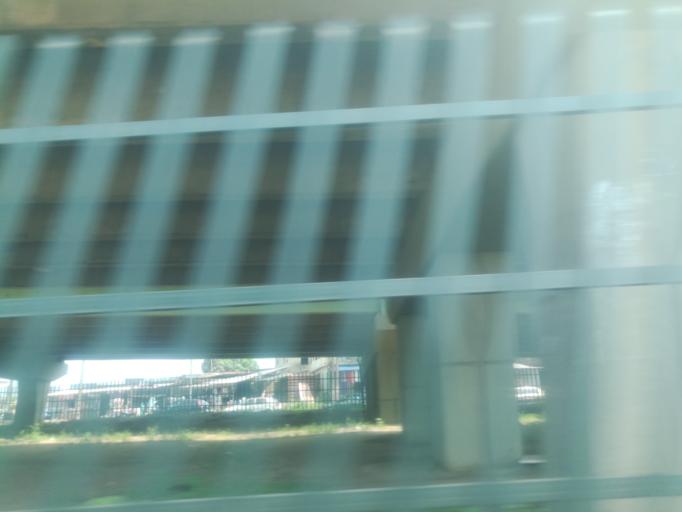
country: NG
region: Ogun
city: Abeokuta
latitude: 7.1469
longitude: 3.3614
